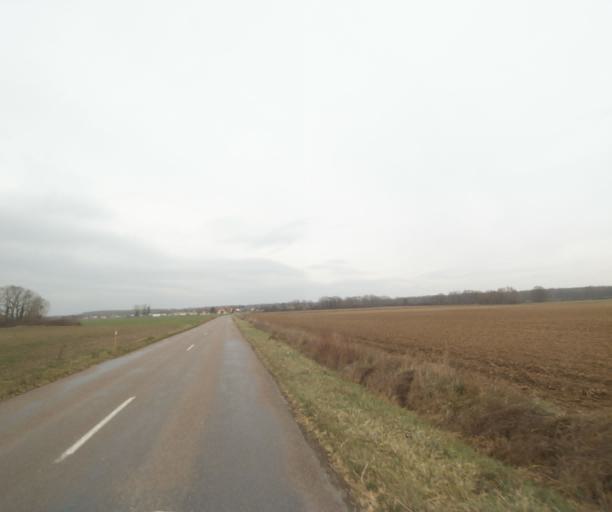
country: FR
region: Champagne-Ardenne
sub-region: Departement de la Haute-Marne
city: Villiers-en-Lieu
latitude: 48.6749
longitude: 4.8890
